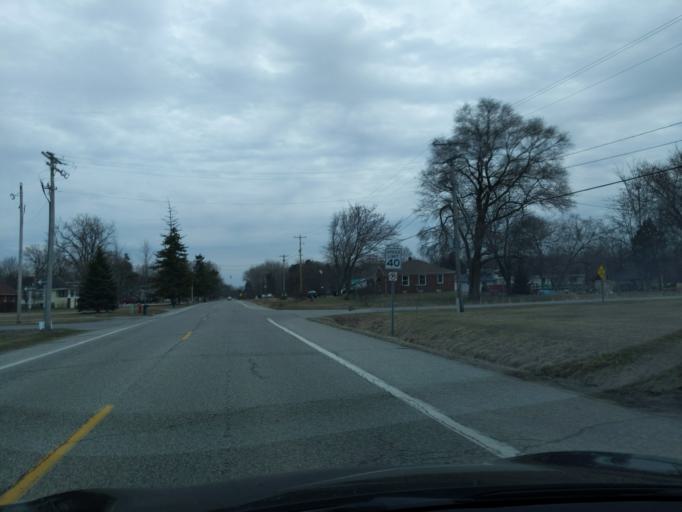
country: US
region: Michigan
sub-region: Bay County
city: Bay City
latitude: 43.6594
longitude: -83.9125
